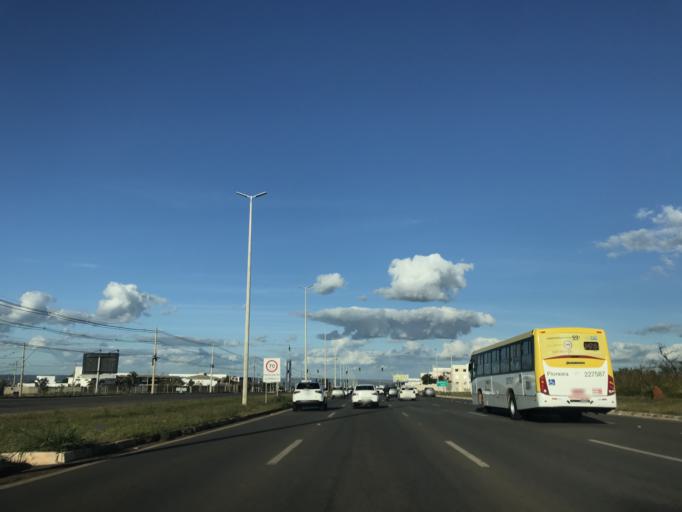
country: BR
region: Federal District
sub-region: Brasilia
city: Brasilia
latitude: -15.8907
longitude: -47.7991
